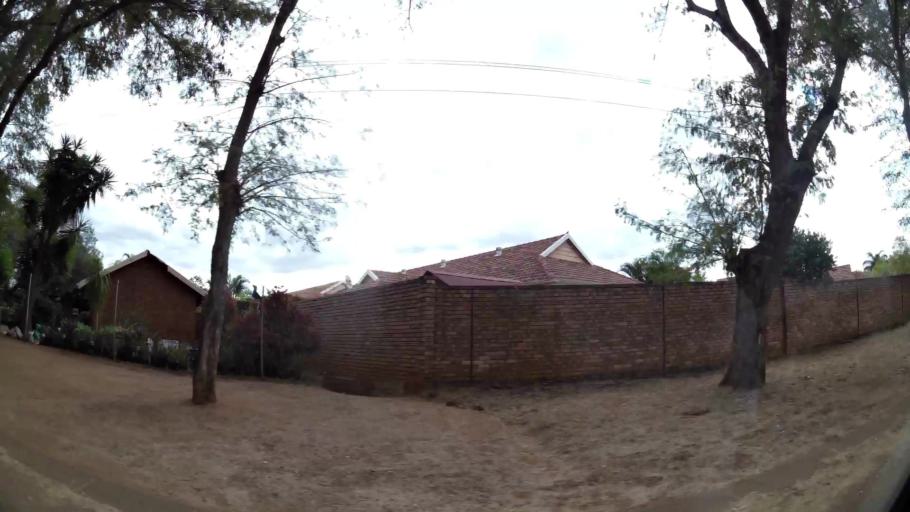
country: ZA
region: Limpopo
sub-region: Waterberg District Municipality
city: Modimolle
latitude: -24.5182
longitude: 28.7033
